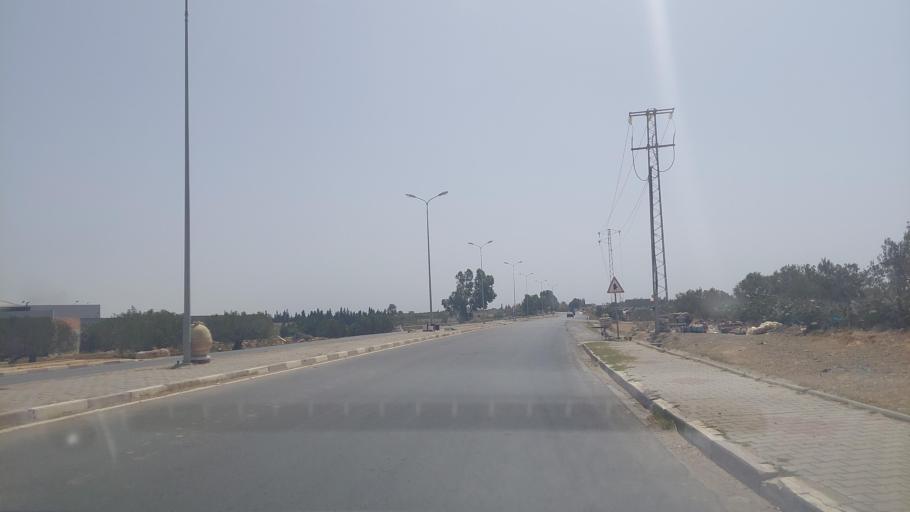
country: TN
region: Al Munastir
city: Qasr Hallal
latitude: 35.6299
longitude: 10.8716
